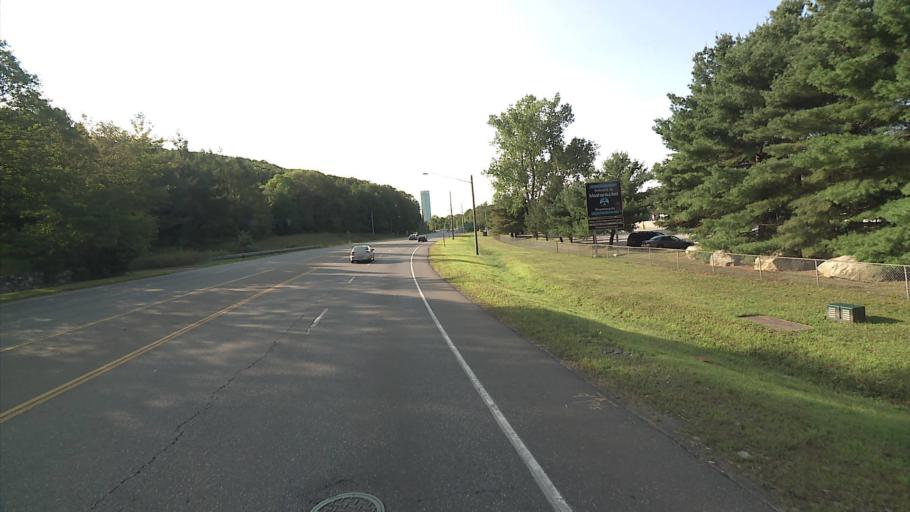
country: US
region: Connecticut
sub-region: New London County
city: Preston City
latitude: 41.4863
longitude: -71.9711
